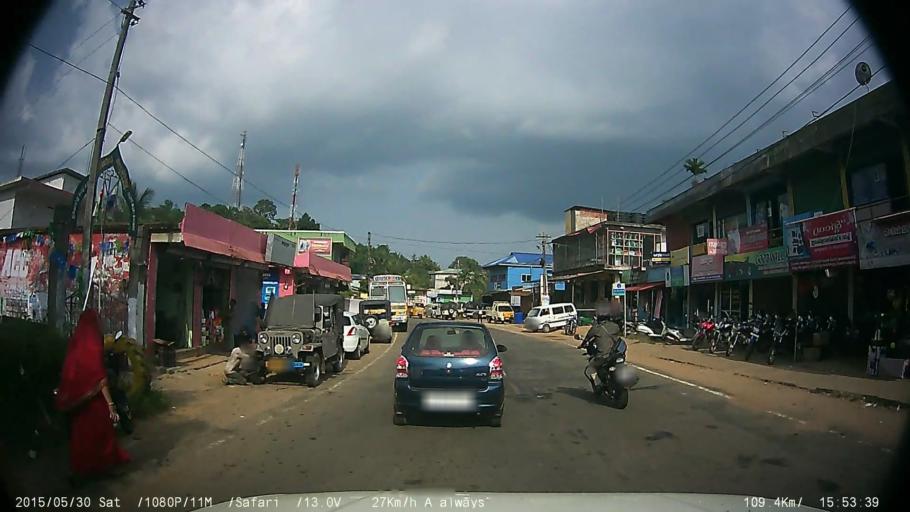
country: IN
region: Kerala
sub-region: Wayanad
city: Kalpetta
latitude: 11.6736
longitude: 76.0769
